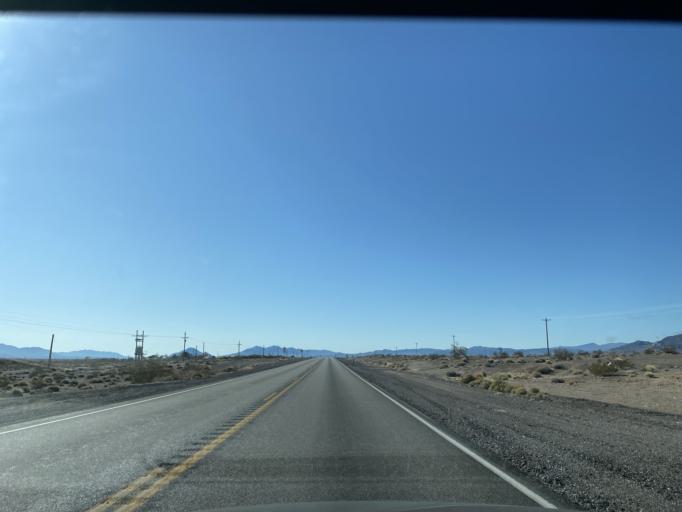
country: US
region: Nevada
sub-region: Nye County
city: Pahrump
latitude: 36.4243
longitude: -116.4222
